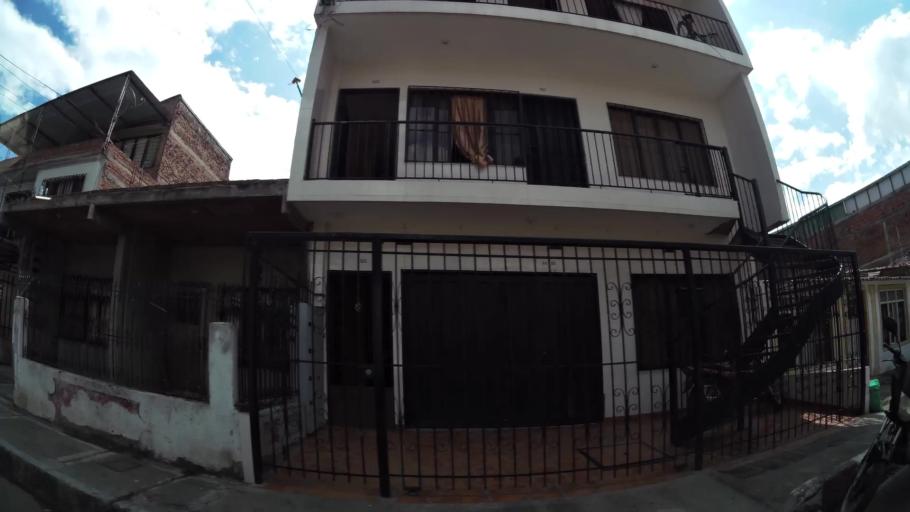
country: CO
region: Valle del Cauca
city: Cali
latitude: 3.4002
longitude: -76.5168
